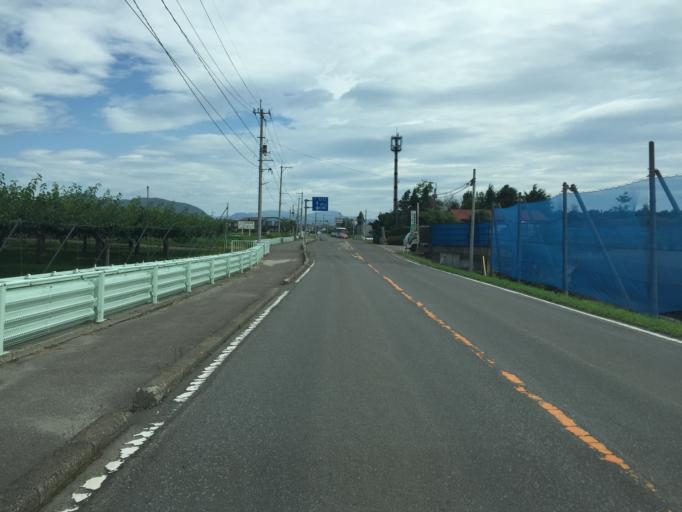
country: JP
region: Fukushima
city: Fukushima-shi
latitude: 37.7664
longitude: 140.3817
